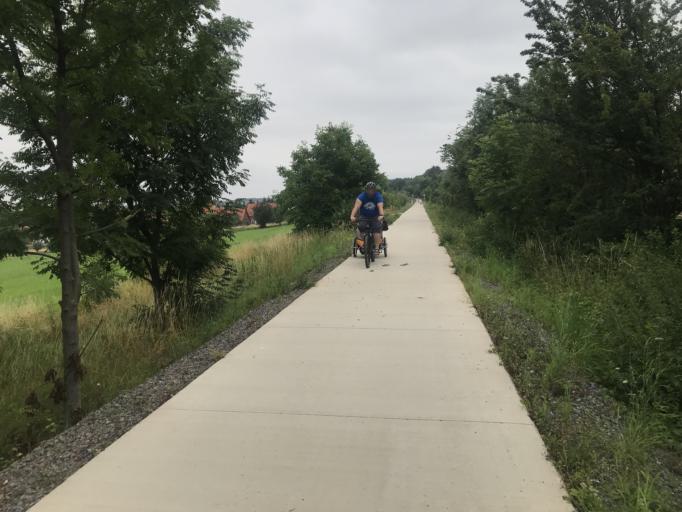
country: DE
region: Saxony-Anhalt
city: Rieder
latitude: 51.7303
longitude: 11.1612
